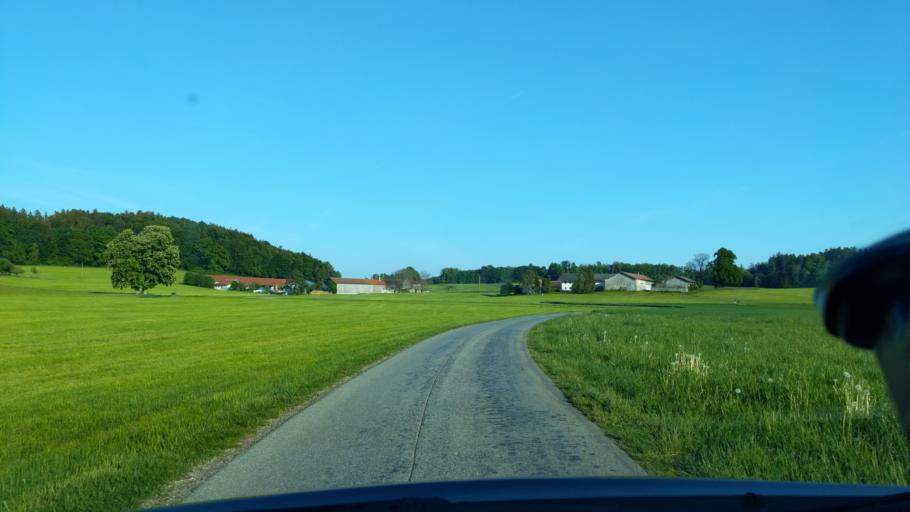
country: DE
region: Bavaria
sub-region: Upper Bavaria
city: Grafing bei Munchen
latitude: 48.0588
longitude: 11.9785
